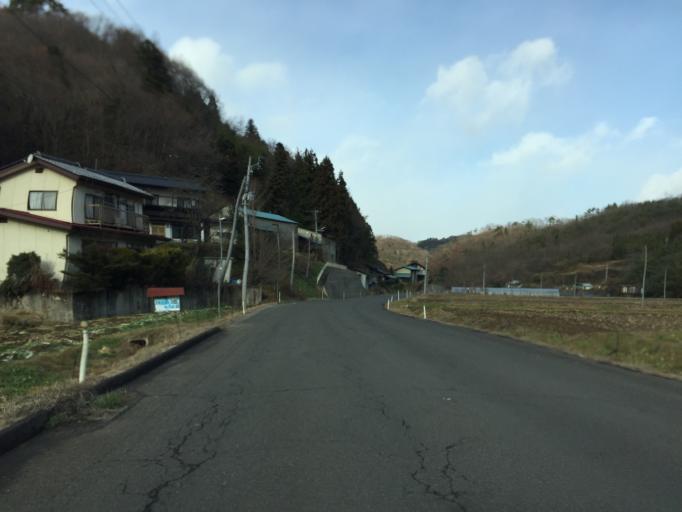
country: JP
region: Fukushima
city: Hobaramachi
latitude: 37.7514
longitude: 140.5589
